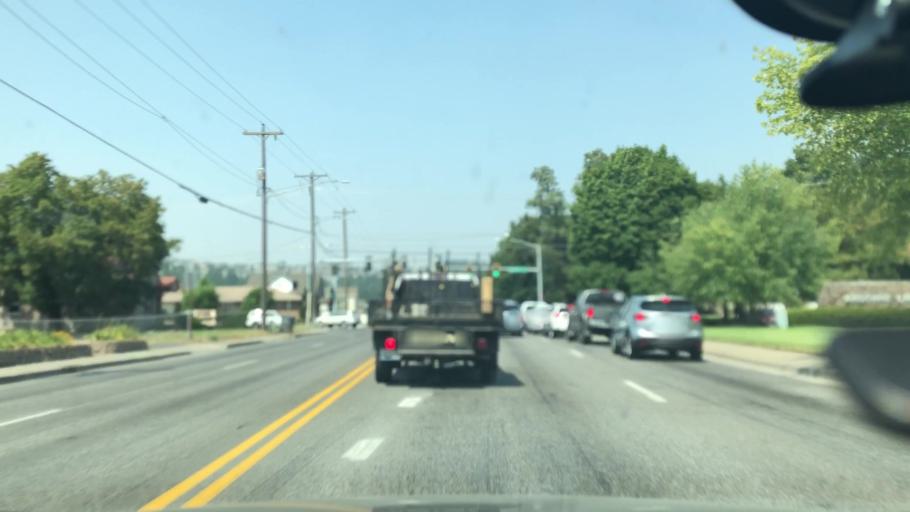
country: US
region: Washington
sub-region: Spokane County
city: Millwood
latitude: 47.6962
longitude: -117.2828
